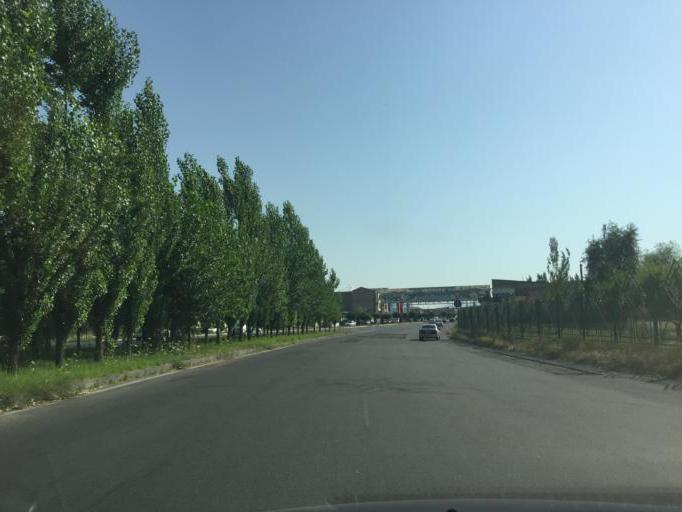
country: AM
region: Kotayk'i Marz
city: Ptghni
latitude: 40.2387
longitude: 44.5665
